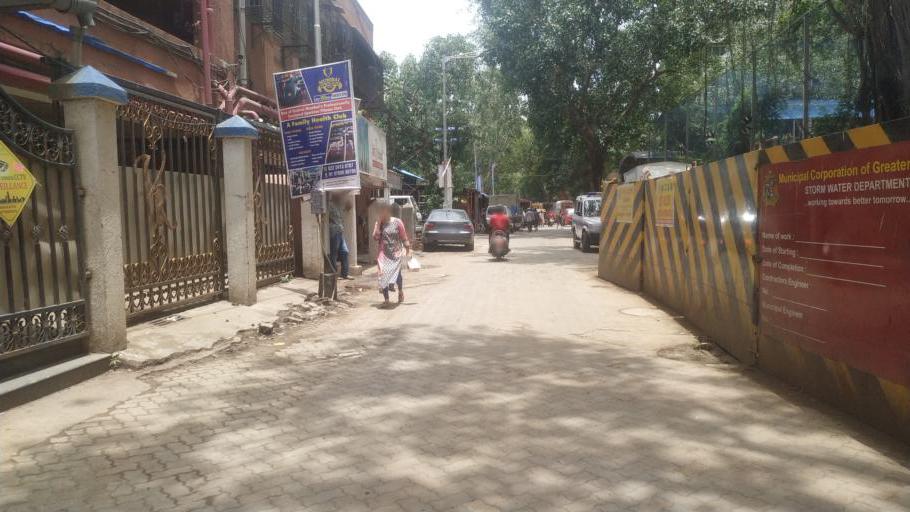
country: IN
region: Maharashtra
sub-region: Mumbai Suburban
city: Mumbai
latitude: 18.9914
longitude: 72.8378
